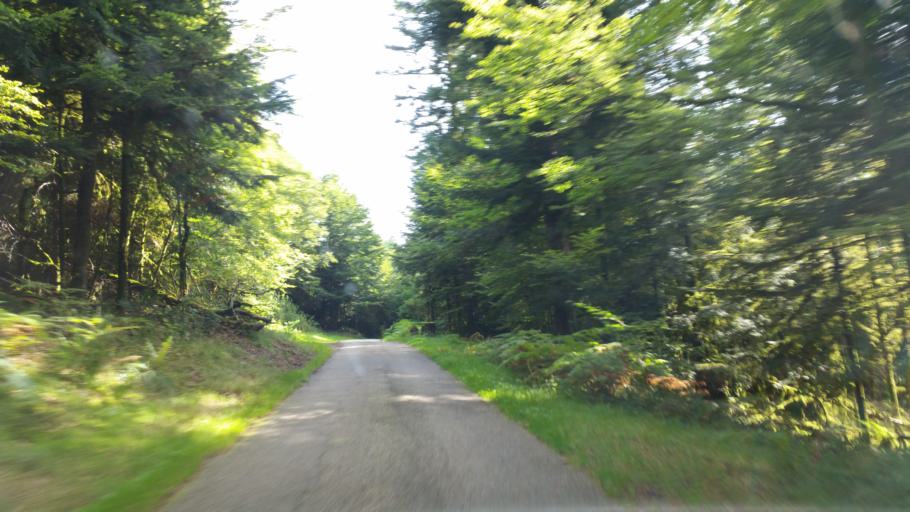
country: FR
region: Lorraine
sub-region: Departement des Vosges
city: Vecoux
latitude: 47.9642
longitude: 6.5864
